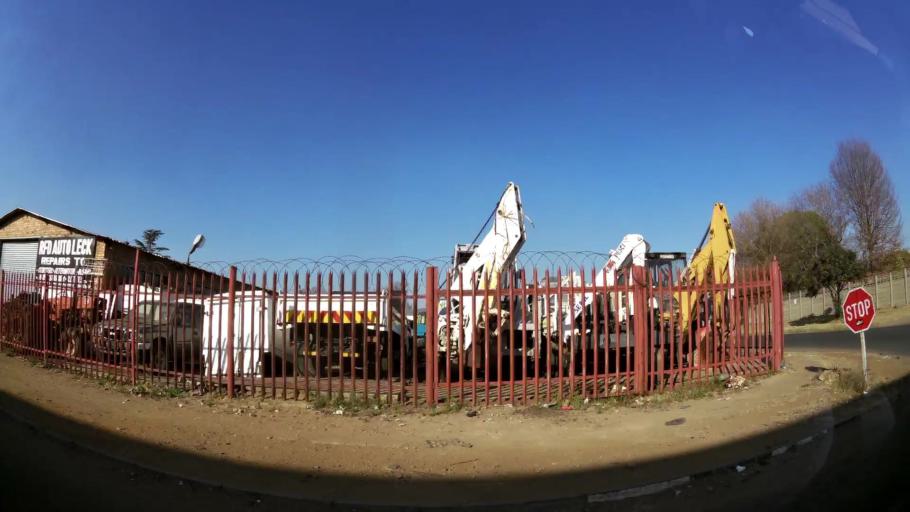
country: ZA
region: Gauteng
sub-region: West Rand District Municipality
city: Randfontein
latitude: -26.1855
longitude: 27.7000
